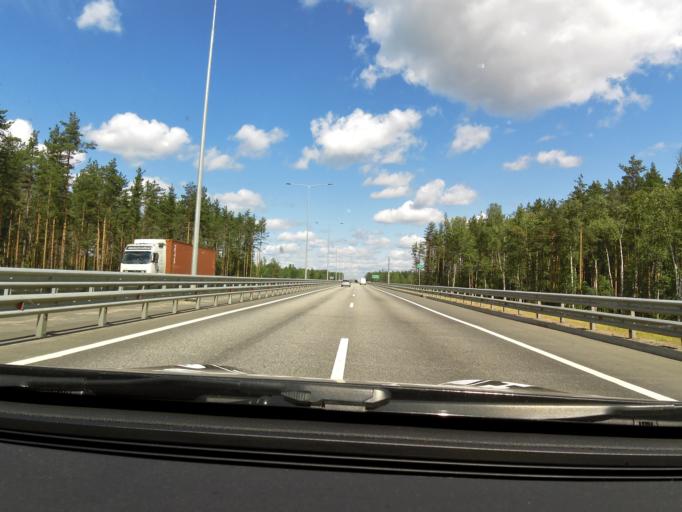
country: RU
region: Tverskaya
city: Krasnomayskiy
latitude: 57.6524
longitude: 34.2339
